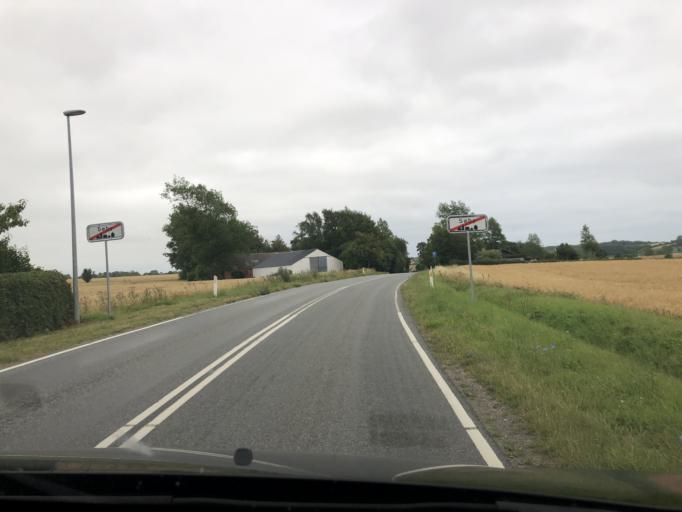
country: DK
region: South Denmark
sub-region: AEro Kommune
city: AEroskobing
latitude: 54.9342
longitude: 10.2640
